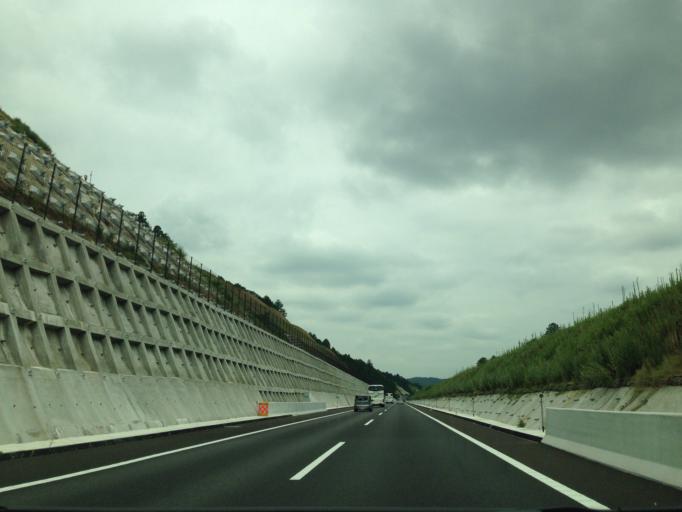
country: JP
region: Aichi
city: Gamagori
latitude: 34.9038
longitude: 137.3089
